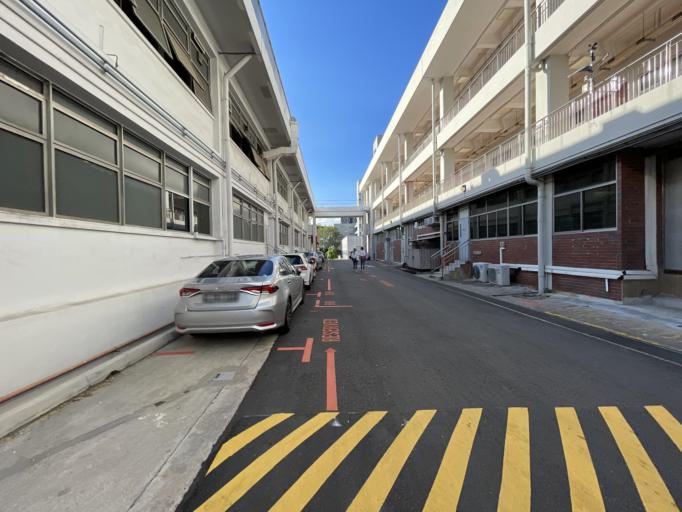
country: SG
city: Singapore
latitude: 1.2985
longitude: 103.7710
